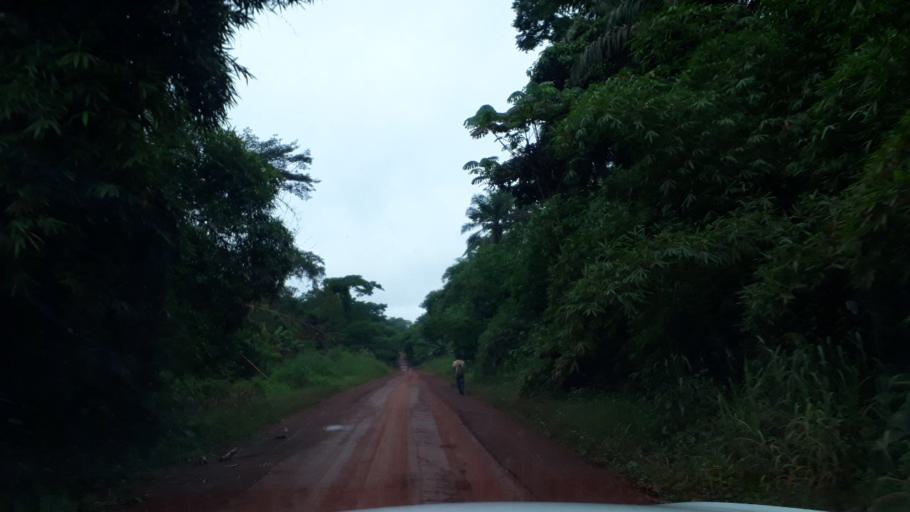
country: CD
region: Eastern Province
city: Wamba
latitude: 1.3580
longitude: 27.5924
